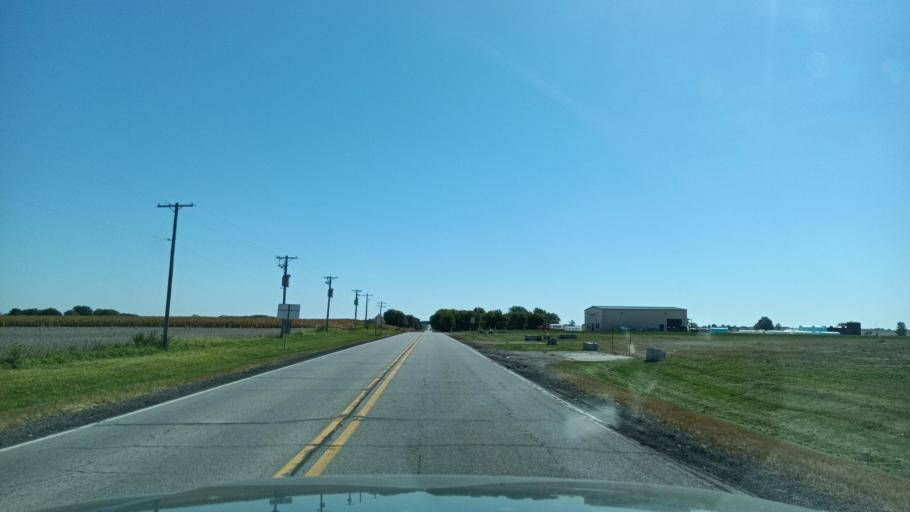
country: US
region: Illinois
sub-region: Peoria County
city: Elmwood
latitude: 40.8307
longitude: -89.8697
